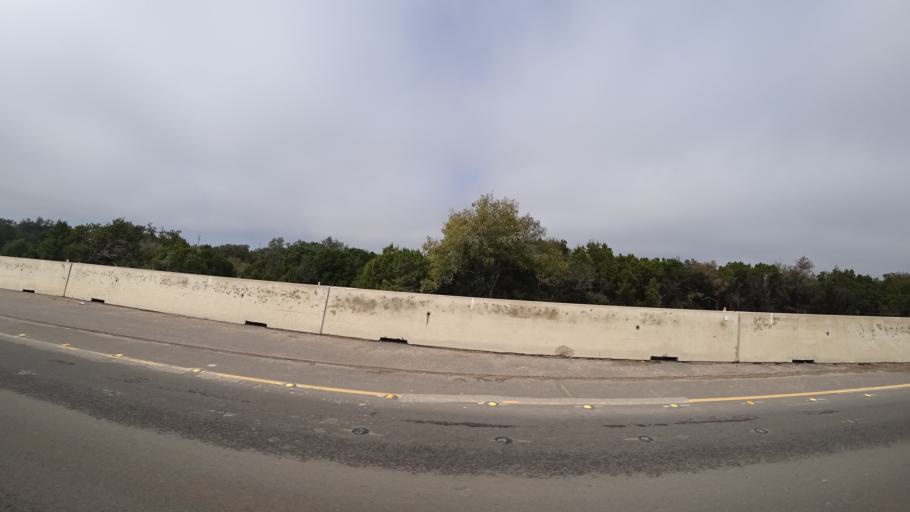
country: US
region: Texas
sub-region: Travis County
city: Shady Hollow
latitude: 30.1764
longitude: -97.8844
